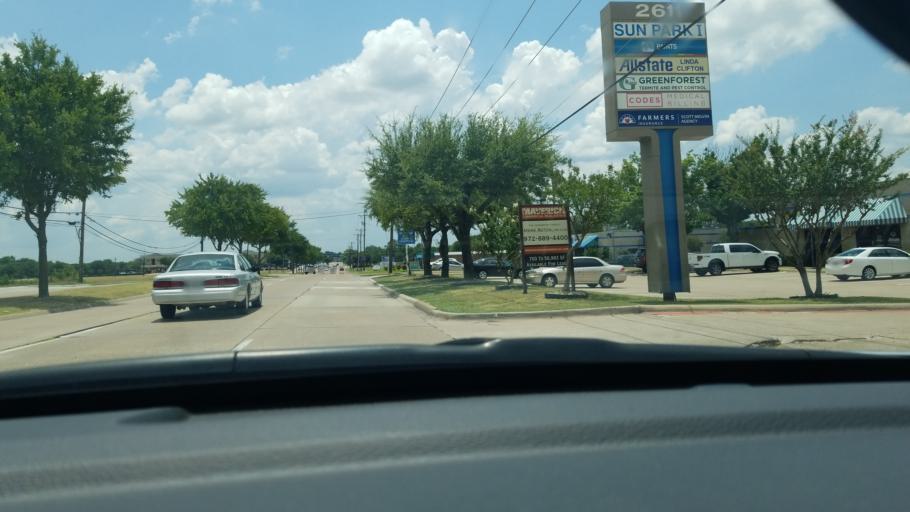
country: US
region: Texas
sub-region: Dallas County
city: Mesquite
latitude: 32.8012
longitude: -96.5959
